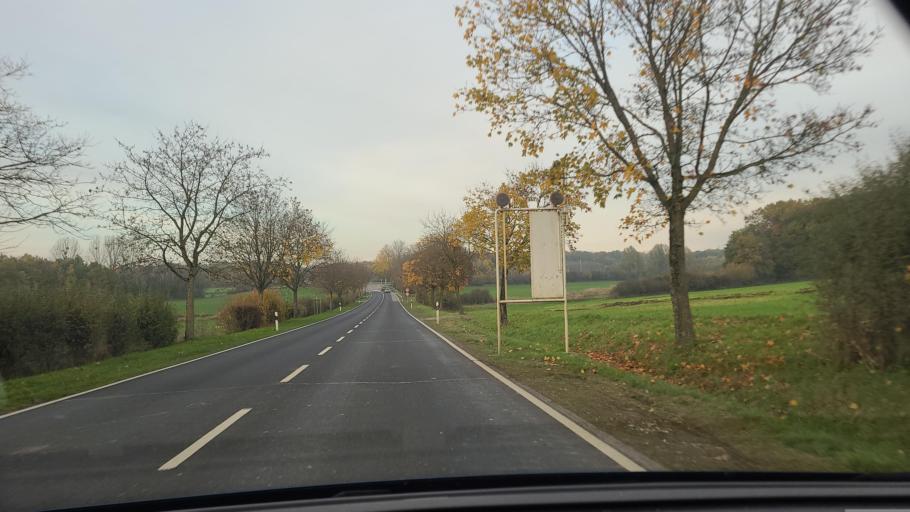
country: LU
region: Luxembourg
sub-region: Canton de Capellen
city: Garnich
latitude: 49.6308
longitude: 5.9562
